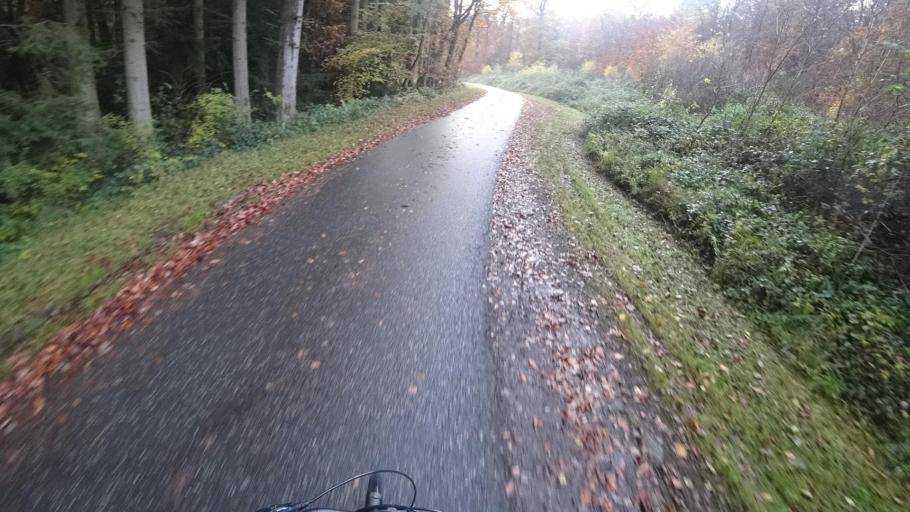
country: DE
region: Rheinland-Pfalz
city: Ney
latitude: 50.1658
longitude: 7.5244
